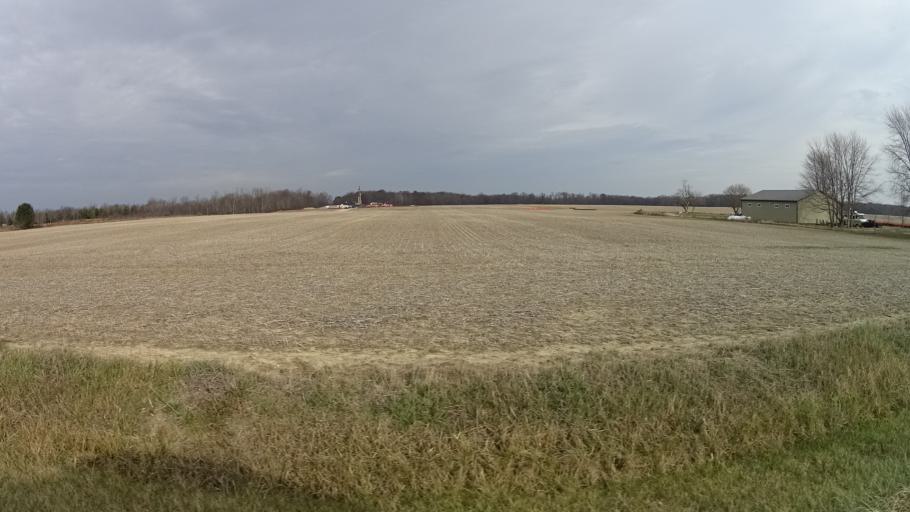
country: US
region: Ohio
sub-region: Lorain County
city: Wellington
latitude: 41.1370
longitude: -82.1644
